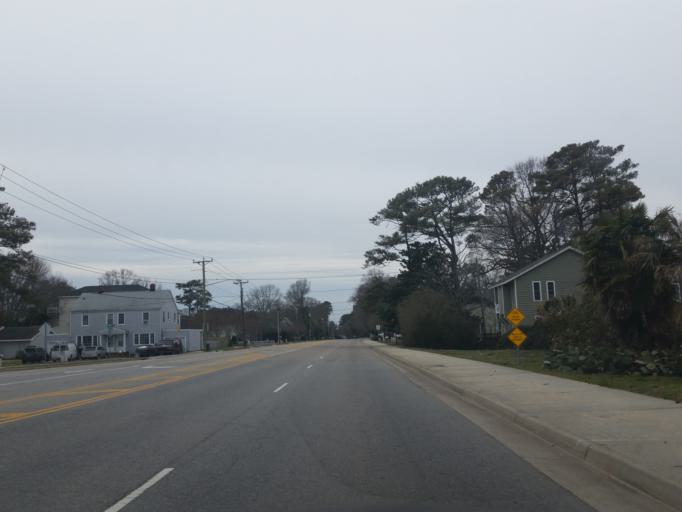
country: US
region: Virginia
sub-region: City of Virginia Beach
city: Virginia Beach
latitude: 36.8289
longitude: -75.9739
